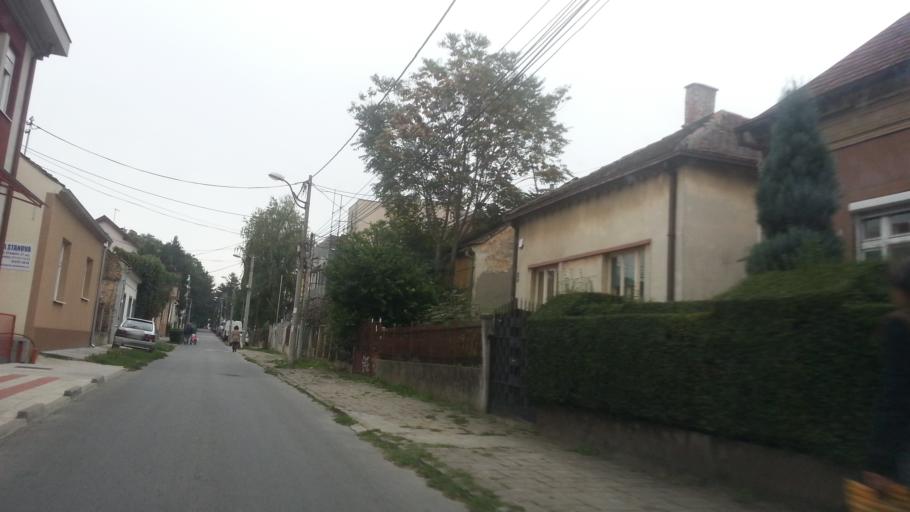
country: RS
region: Central Serbia
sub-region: Belgrade
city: Zemun
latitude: 44.8408
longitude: 20.3982
